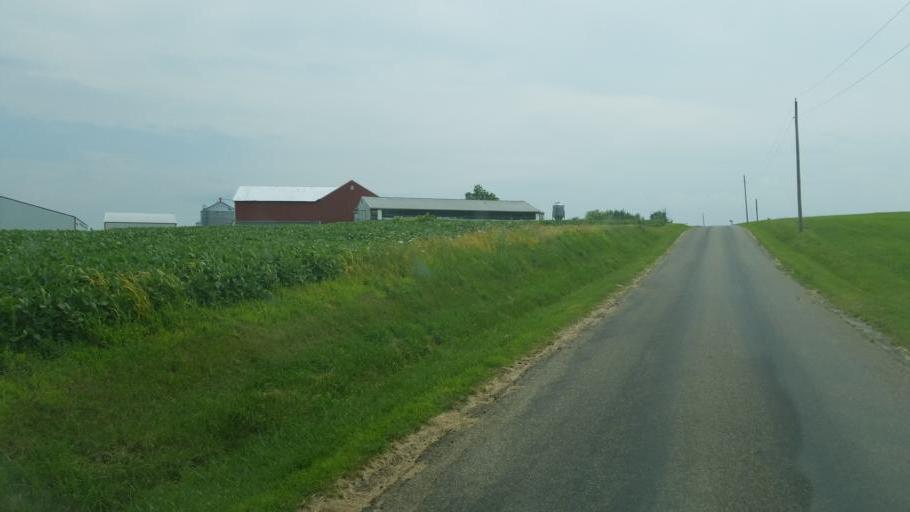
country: US
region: Ohio
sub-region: Richland County
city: Lexington
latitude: 40.6802
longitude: -82.6300
